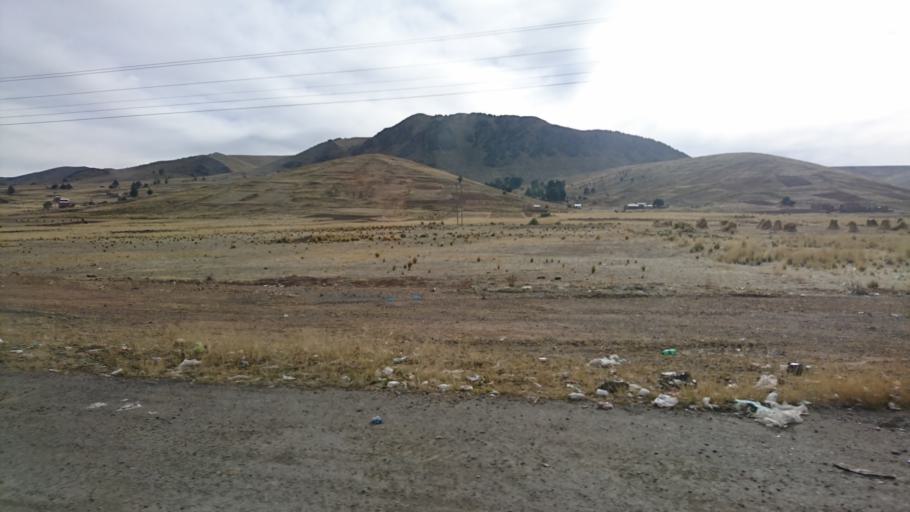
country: BO
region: La Paz
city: La Paz
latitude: -16.4167
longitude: -68.3428
